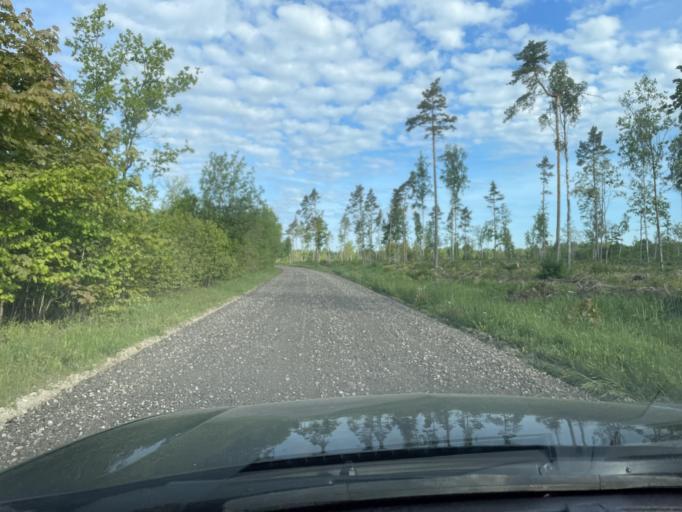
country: EE
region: Harju
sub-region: Keila linn
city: Keila
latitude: 59.3061
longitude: 24.2961
